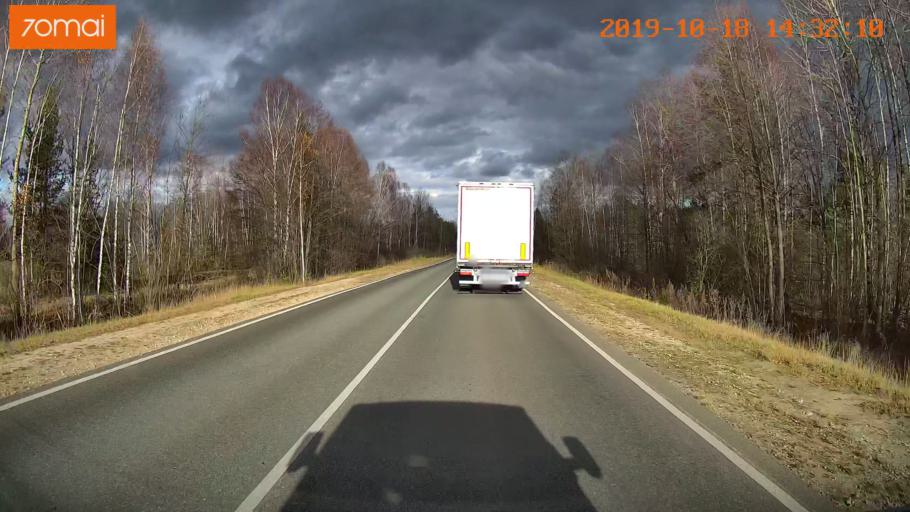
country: RU
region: Rjazan
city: Tuma
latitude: 55.1888
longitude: 40.5757
